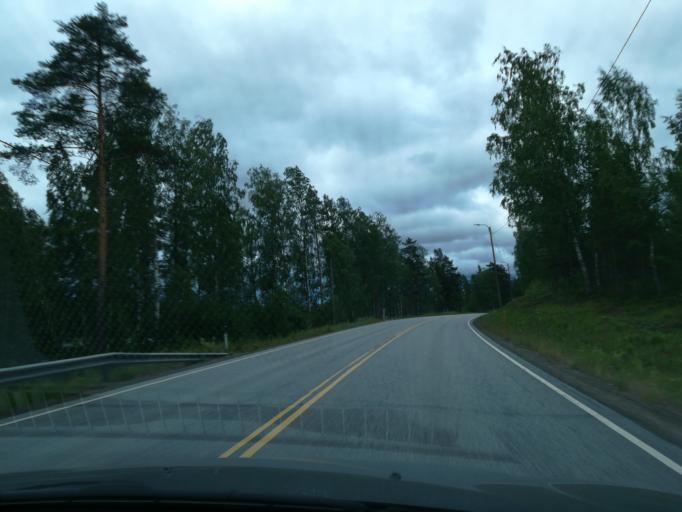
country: FI
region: Southern Savonia
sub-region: Mikkeli
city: Ristiina
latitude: 61.3514
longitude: 27.3883
